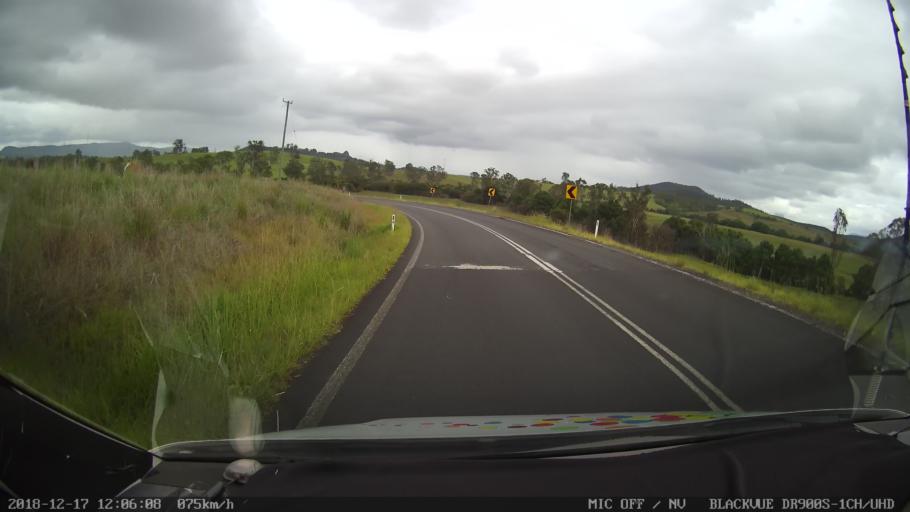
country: AU
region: New South Wales
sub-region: Kyogle
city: Kyogle
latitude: -28.4855
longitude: 152.5683
